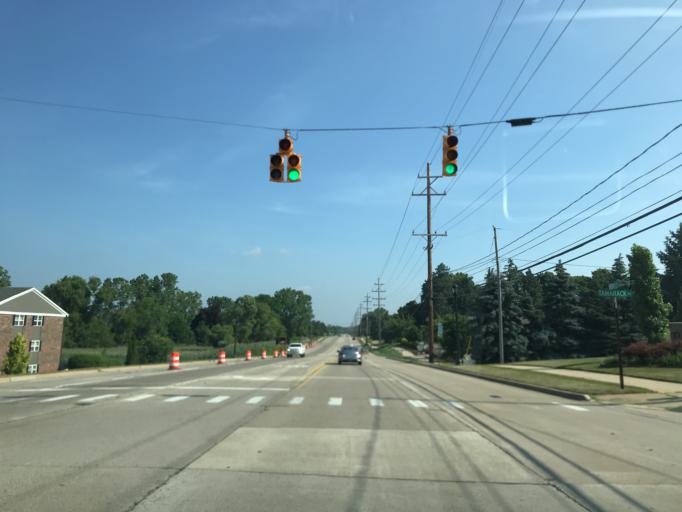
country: US
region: Michigan
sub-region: Ingham County
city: Okemos
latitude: 42.6909
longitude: -84.4323
